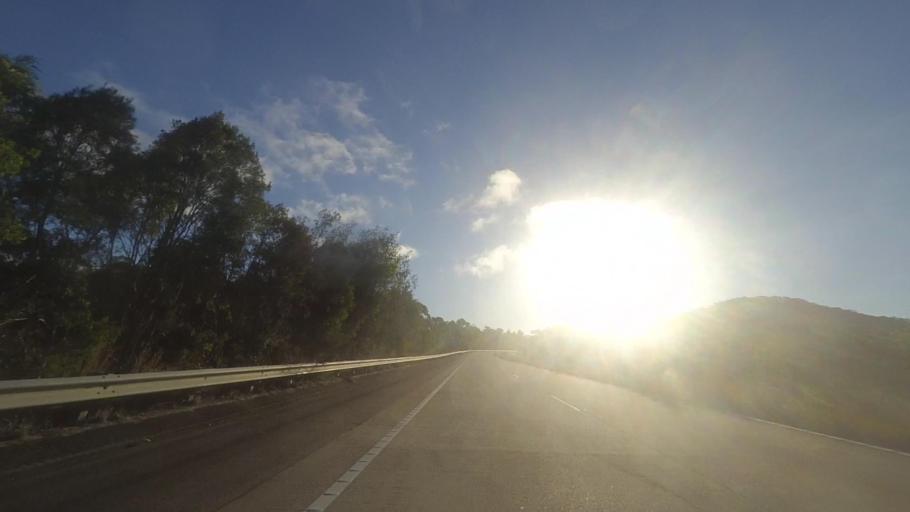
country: AU
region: New South Wales
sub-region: Great Lakes
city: Bulahdelah
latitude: -32.3851
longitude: 152.2613
